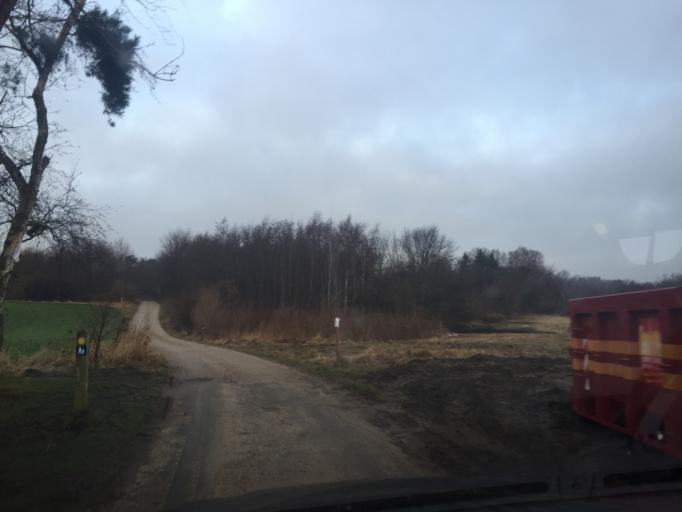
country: DK
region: Capital Region
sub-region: Hoje-Taastrup Kommune
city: Flong
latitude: 55.6843
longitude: 12.2349
